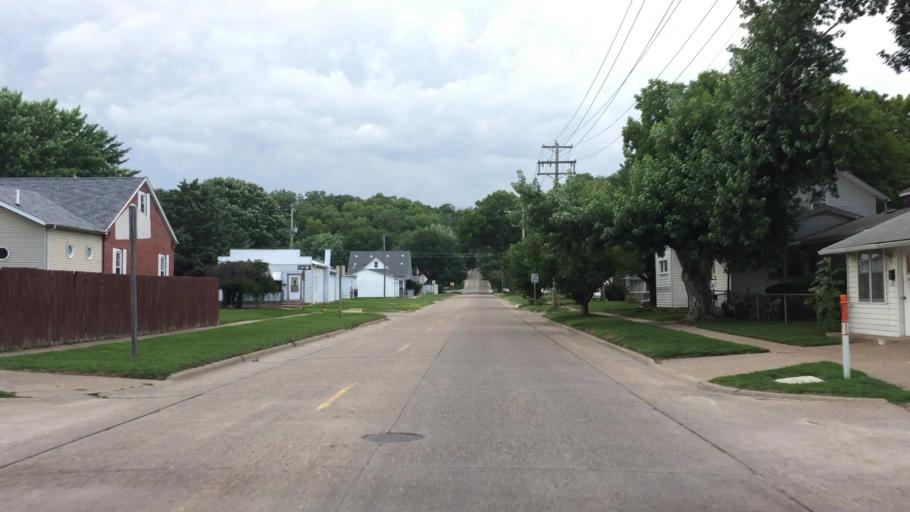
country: US
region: Iowa
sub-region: Lee County
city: Fort Madison
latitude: 40.6336
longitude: -91.3246
